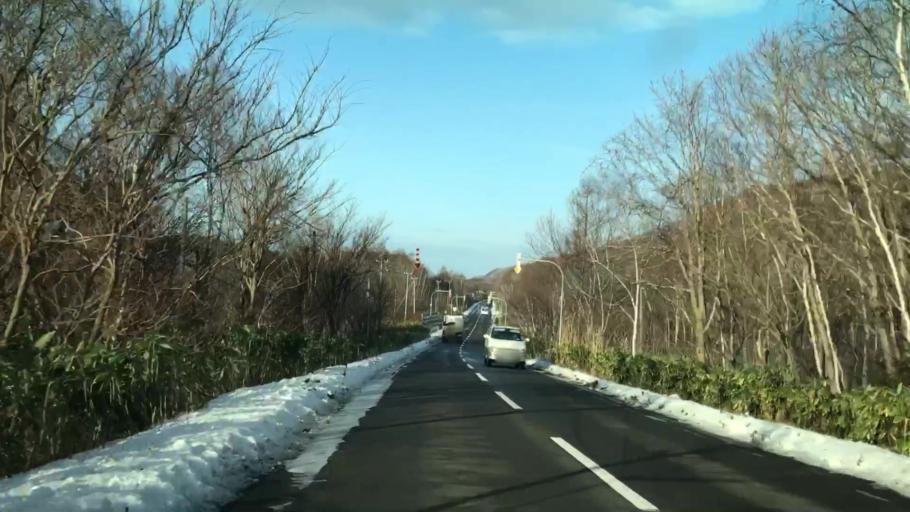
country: JP
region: Hokkaido
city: Yoichi
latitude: 43.3173
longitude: 140.5301
